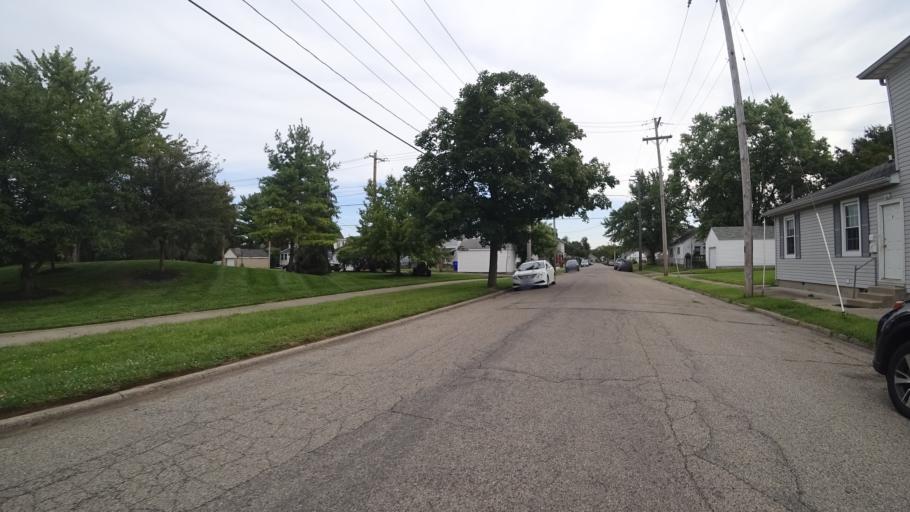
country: US
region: Ohio
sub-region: Butler County
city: Hamilton
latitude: 39.3946
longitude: -84.5457
